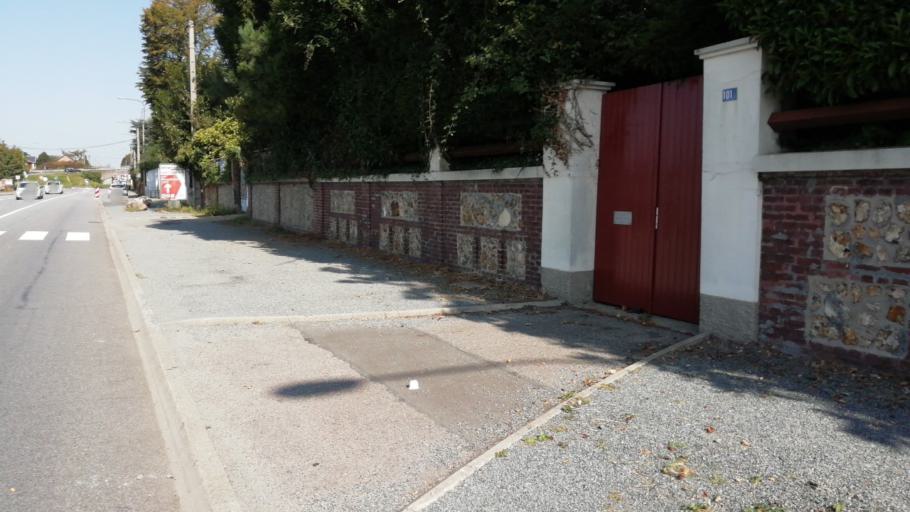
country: FR
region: Haute-Normandie
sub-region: Departement de la Seine-Maritime
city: Montivilliers
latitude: 49.5317
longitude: 0.1897
